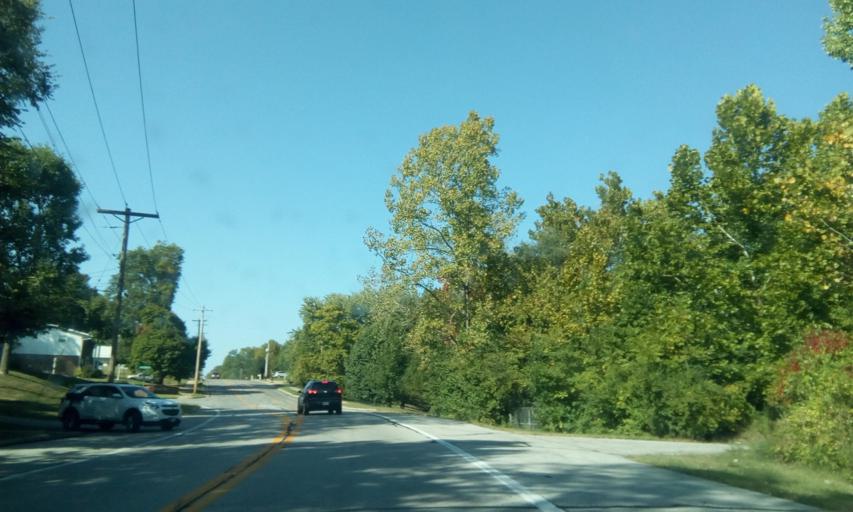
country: US
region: Missouri
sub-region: Saint Louis County
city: Green Park
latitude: 38.5067
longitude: -90.3429
